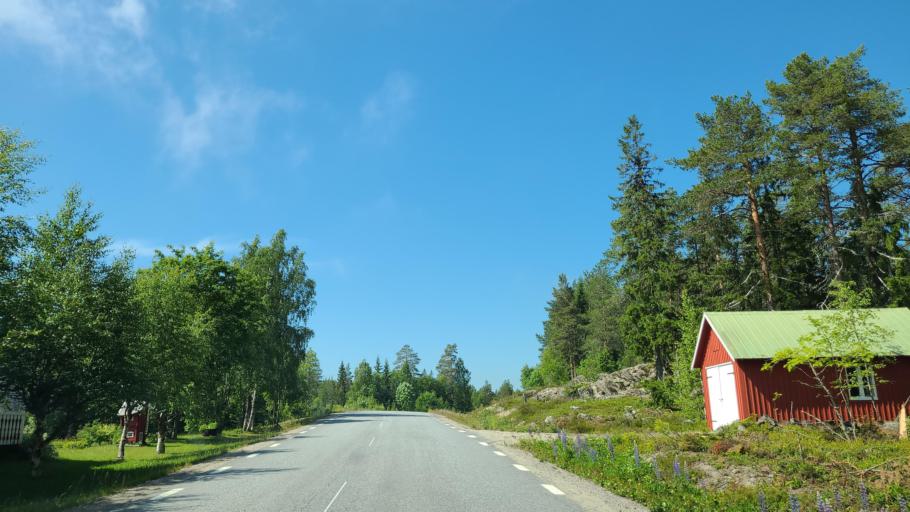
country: SE
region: Vaesternorrland
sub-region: OErnskoeldsviks Kommun
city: Husum
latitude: 63.4809
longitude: 19.2127
